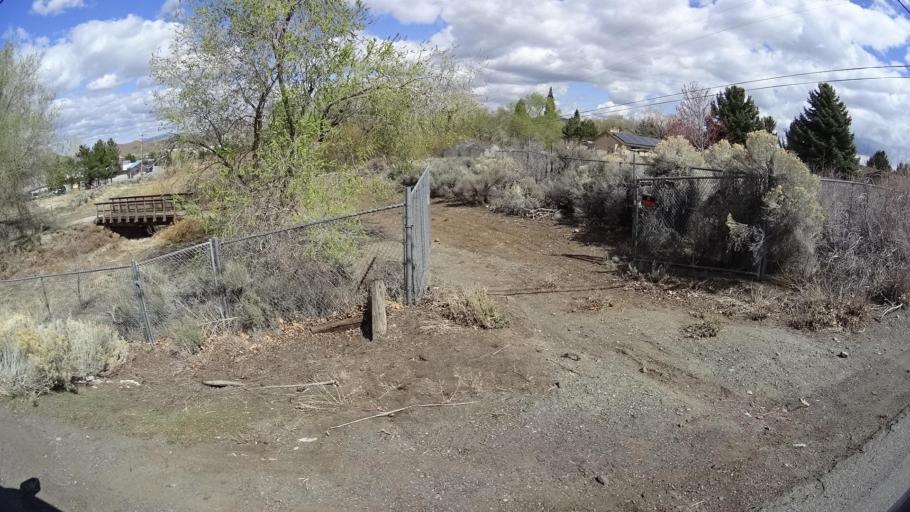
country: US
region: Nevada
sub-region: Washoe County
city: Reno
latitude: 39.4302
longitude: -119.7757
